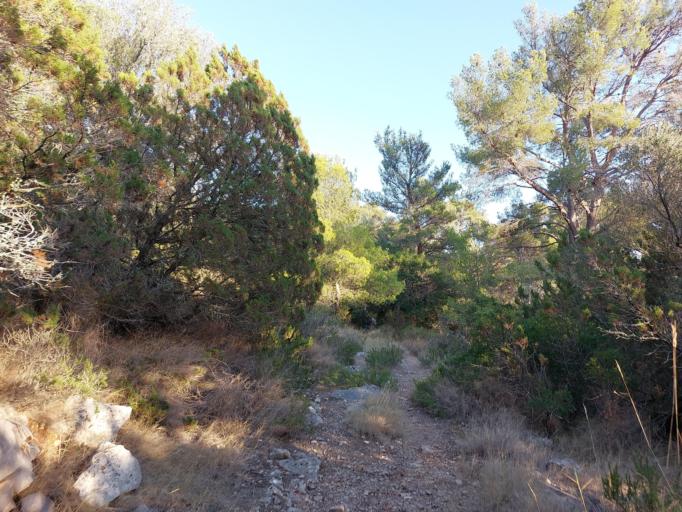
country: HR
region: Dubrovacko-Neretvanska
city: Smokvica
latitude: 42.7741
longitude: 16.7882
